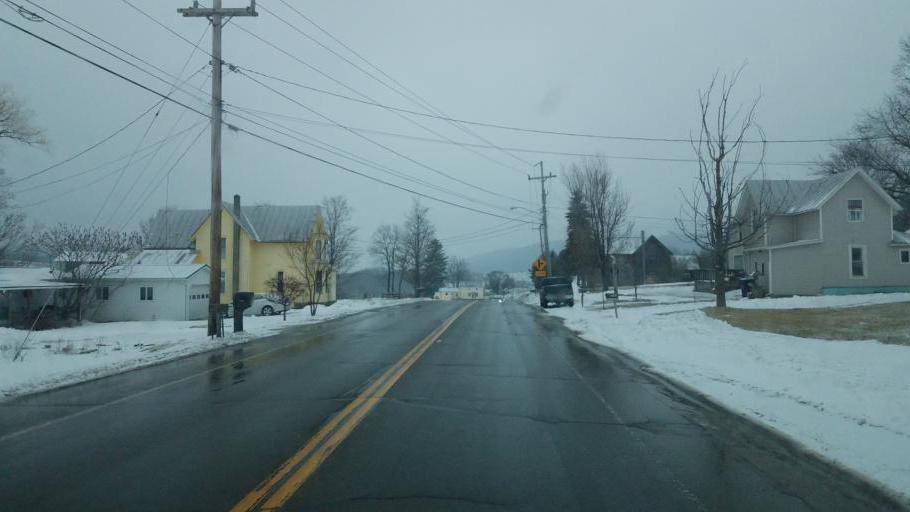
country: US
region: New York
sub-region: Steuben County
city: Canisteo
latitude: 42.1190
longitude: -77.4983
